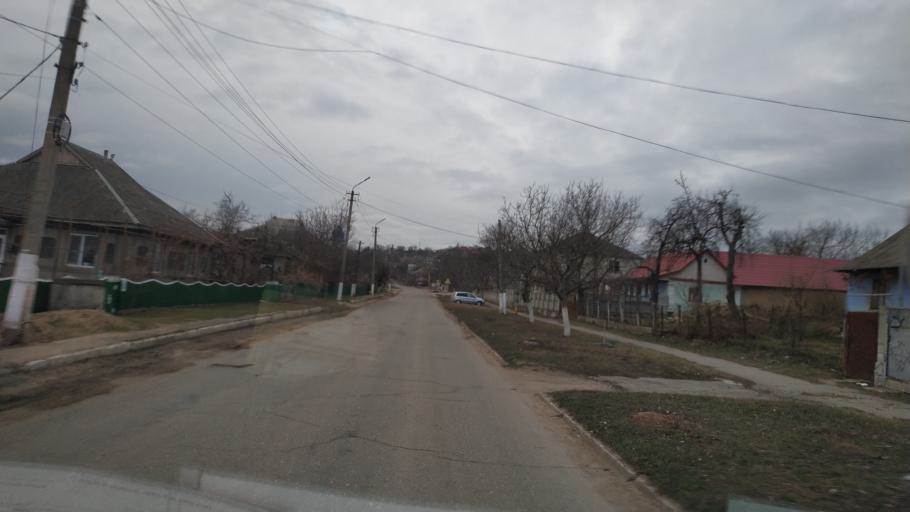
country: MD
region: Causeni
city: Causeni
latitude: 46.6353
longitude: 29.4041
